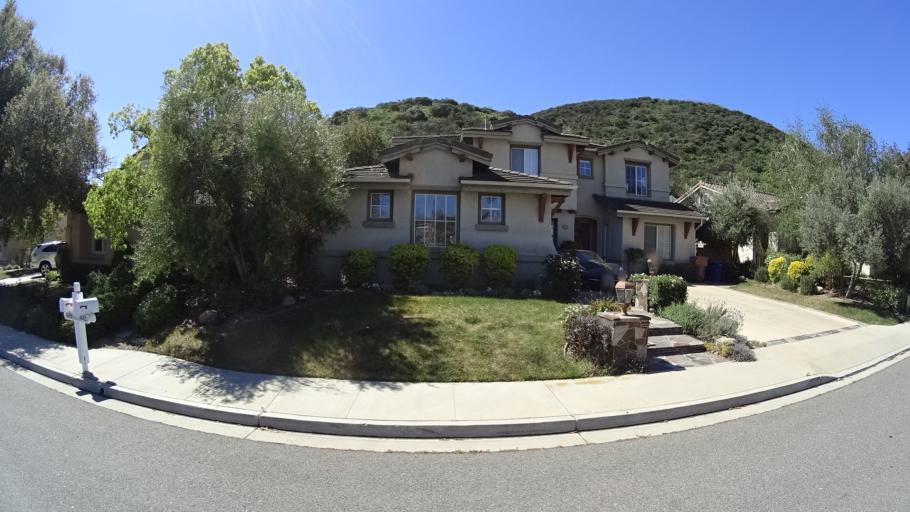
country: US
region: California
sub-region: Ventura County
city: Casa Conejo
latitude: 34.1649
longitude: -118.9748
